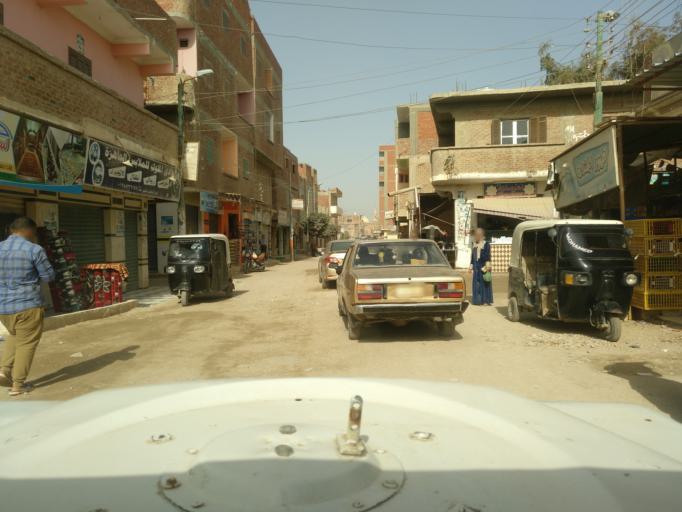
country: EG
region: Al Buhayrah
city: Beheira
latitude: 30.3736
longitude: 30.3516
